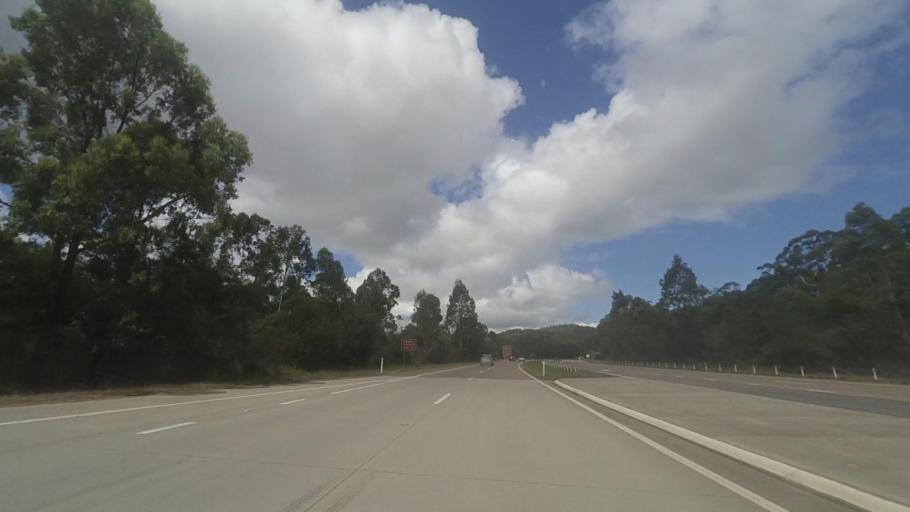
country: AU
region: New South Wales
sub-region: Great Lakes
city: Bulahdelah
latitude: -32.3863
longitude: 152.2299
